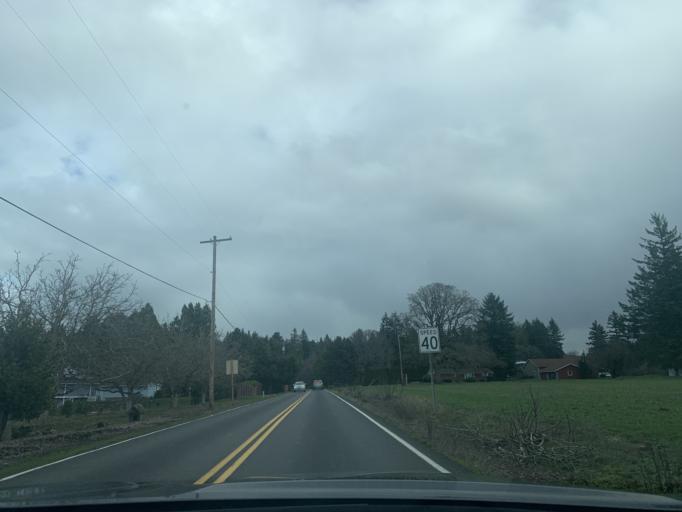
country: US
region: Oregon
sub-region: Washington County
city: Oak Hills
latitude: 45.5674
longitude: -122.8218
